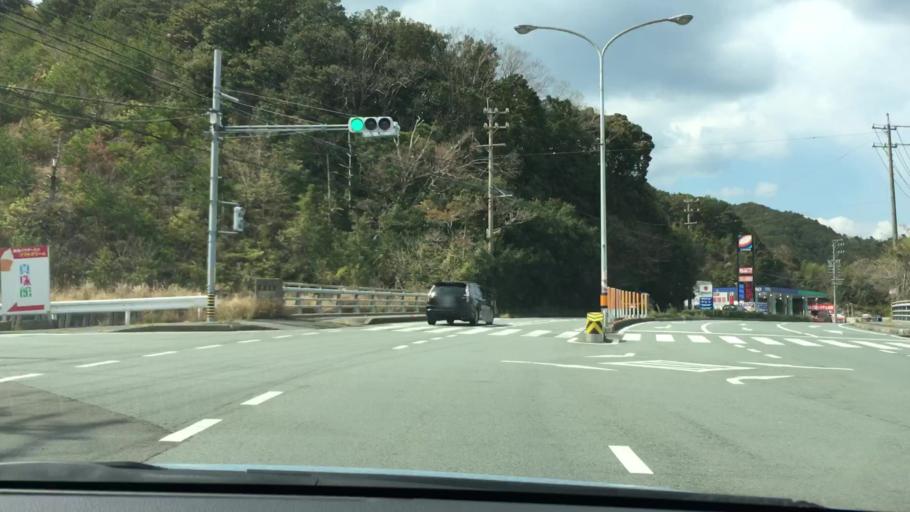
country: JP
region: Mie
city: Toba
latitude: 34.4817
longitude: 136.8166
